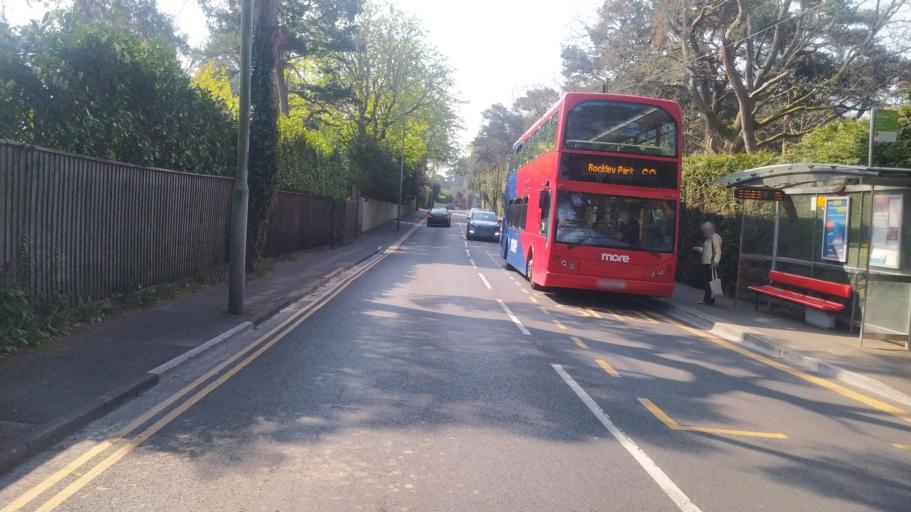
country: GB
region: England
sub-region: Dorset
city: Parkstone
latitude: 50.7068
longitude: -1.9251
